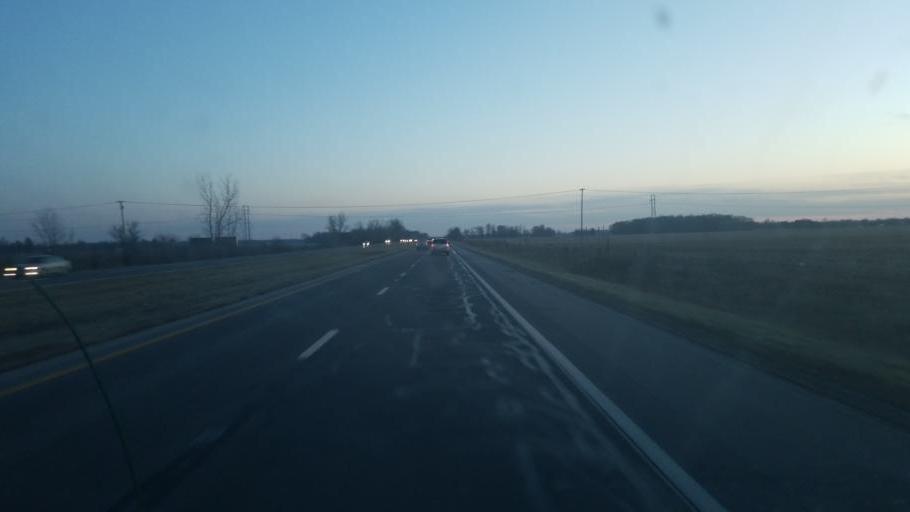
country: US
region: Ohio
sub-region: Marion County
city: Marion
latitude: 40.5118
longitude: -83.0749
